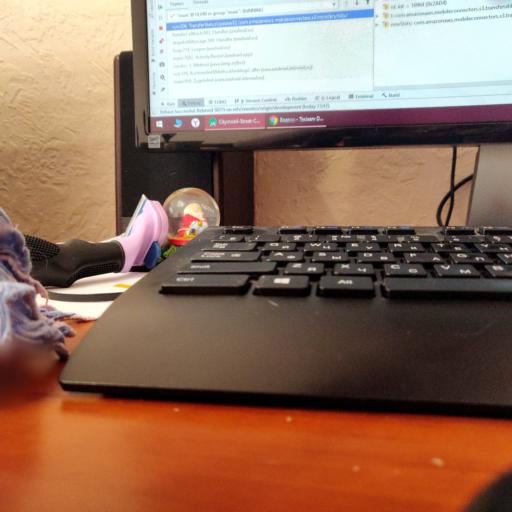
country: FI
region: Haeme
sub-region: Forssa
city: Humppila
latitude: 60.9160
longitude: 23.4339
